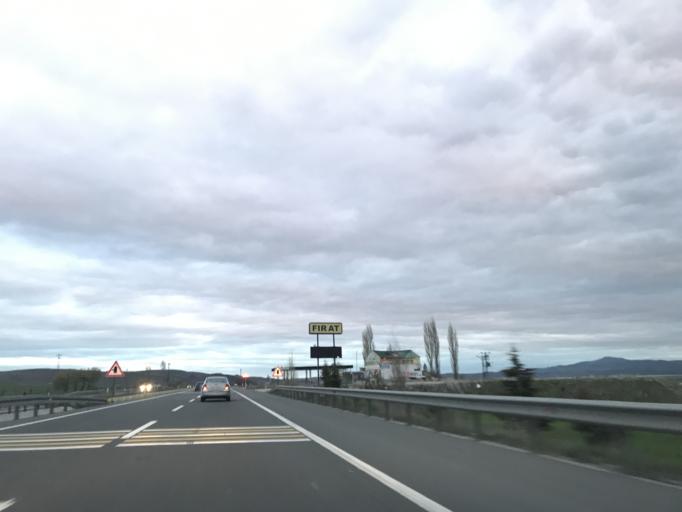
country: TR
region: Ankara
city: Altpinar
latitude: 39.3832
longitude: 32.8915
